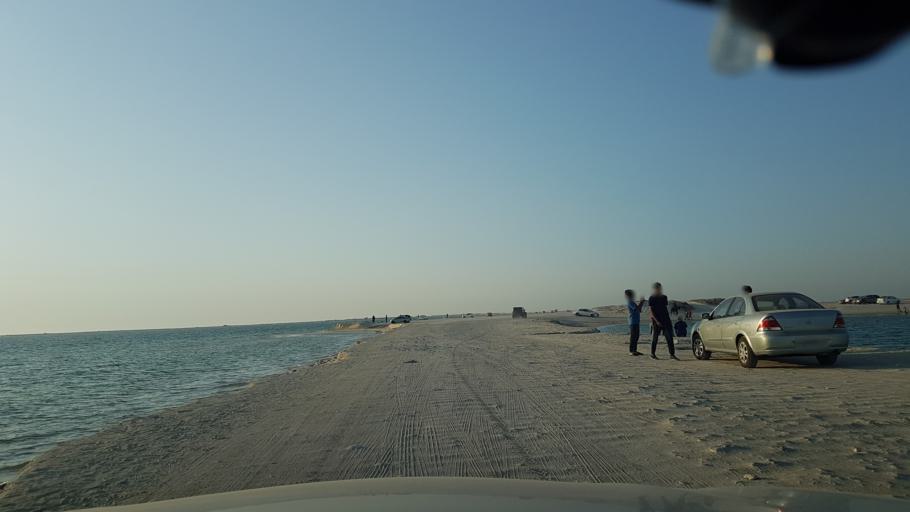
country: BH
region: Manama
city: Jidd Hafs
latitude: 26.2402
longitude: 50.5032
